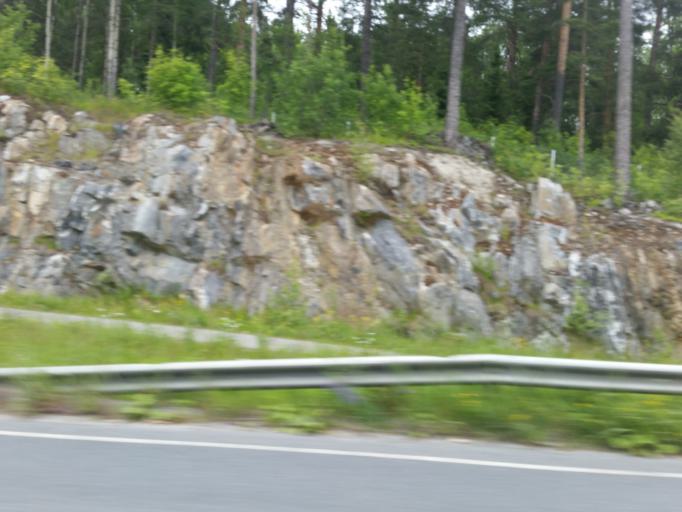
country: FI
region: Northern Savo
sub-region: Kuopio
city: Kuopio
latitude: 62.8829
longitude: 27.6476
